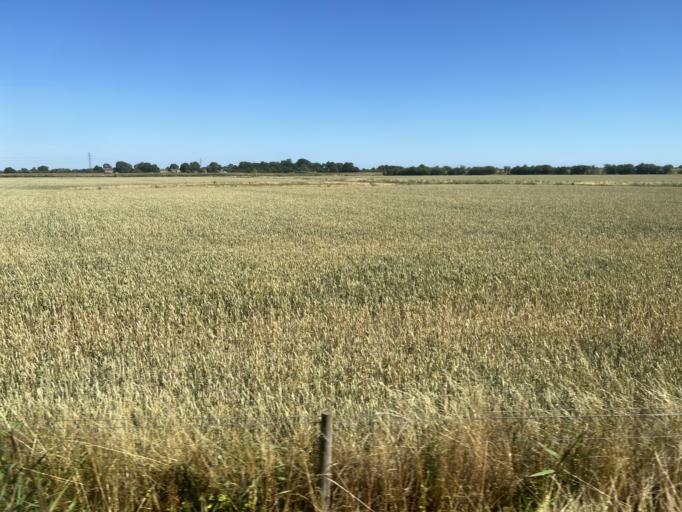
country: GB
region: England
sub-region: Lincolnshire
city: Wainfleet All Saints
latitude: 53.1166
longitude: 0.2101
